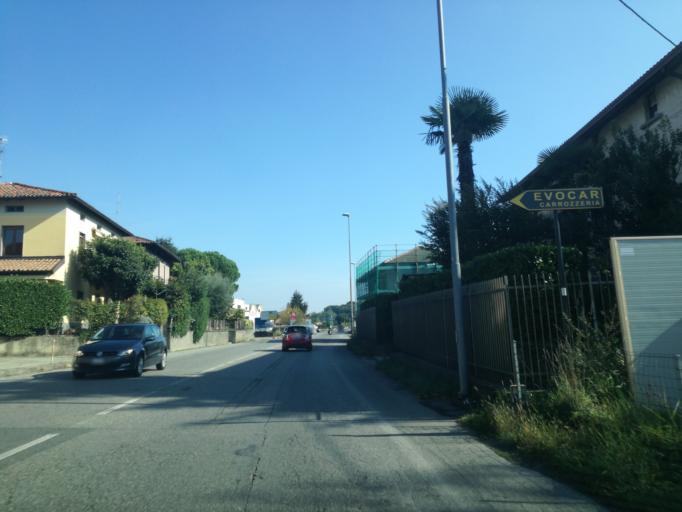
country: IT
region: Lombardy
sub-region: Provincia di Bergamo
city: Gromlongo
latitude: 45.7292
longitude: 9.5297
